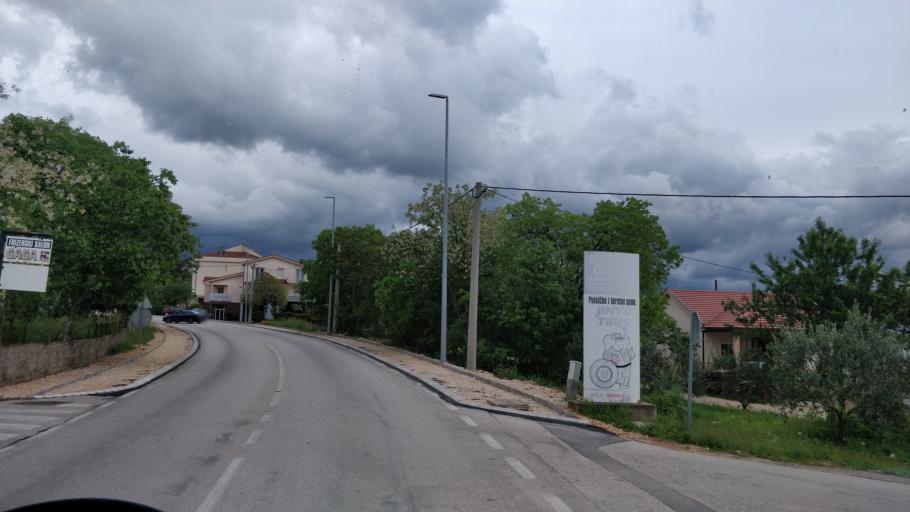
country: BA
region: Federation of Bosnia and Herzegovina
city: Ljubuski
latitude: 43.1886
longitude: 17.5376
